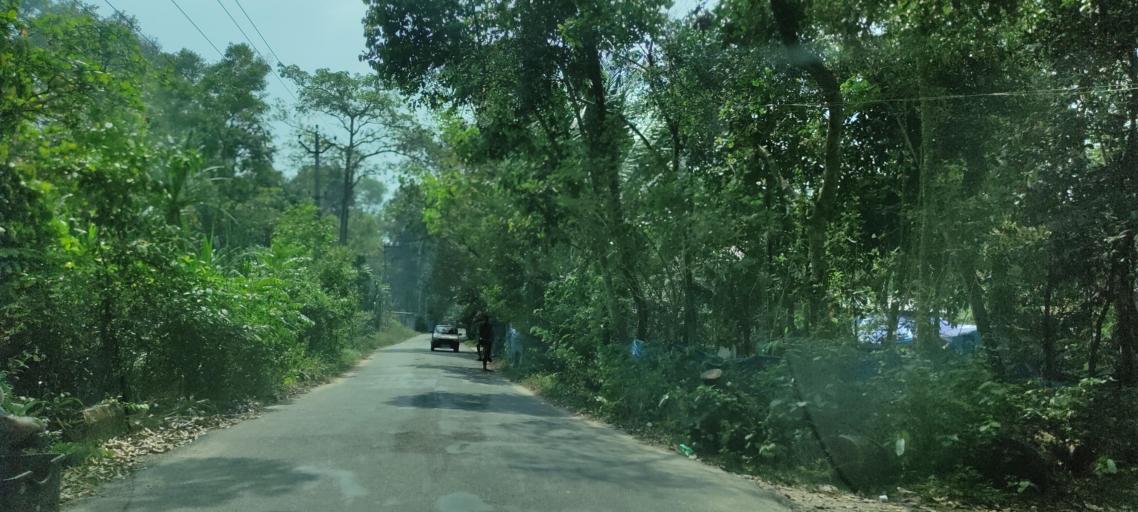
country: IN
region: Kerala
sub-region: Alappuzha
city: Shertallai
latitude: 9.6262
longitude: 76.3504
